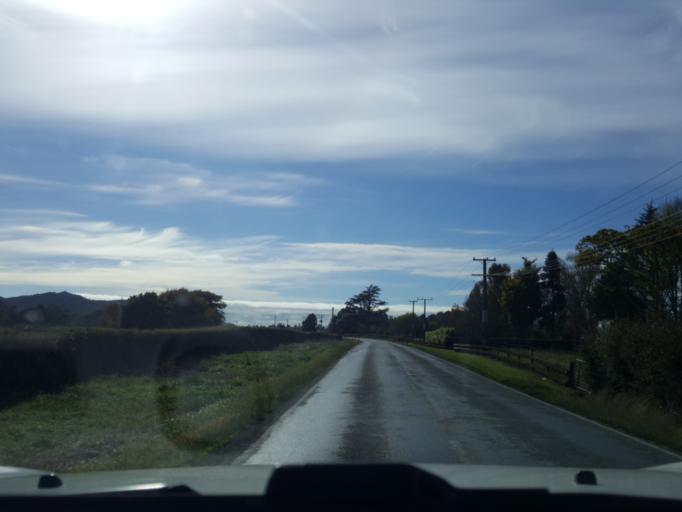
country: NZ
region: Waikato
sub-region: Waikato District
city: Ngaruawahia
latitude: -37.6028
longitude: 175.2007
